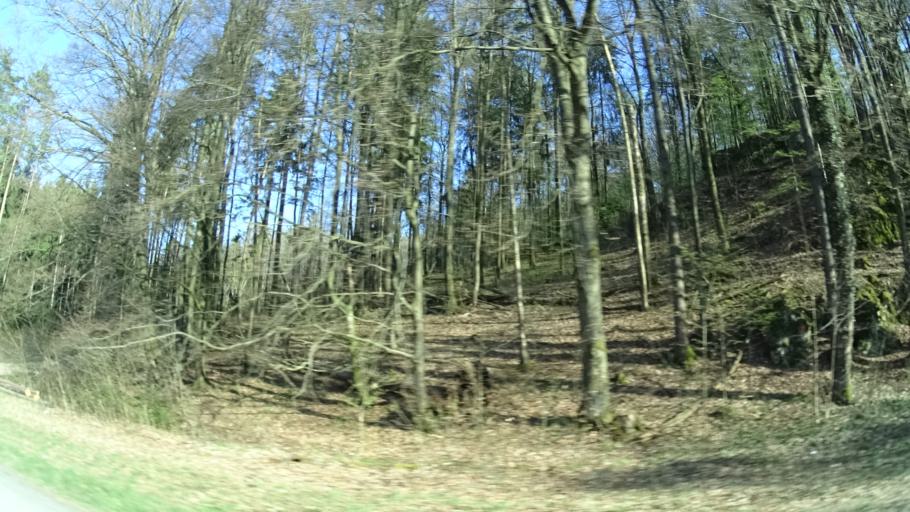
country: DE
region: Bavaria
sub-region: Upper Palatinate
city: Auerbach
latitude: 49.6620
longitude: 11.6340
